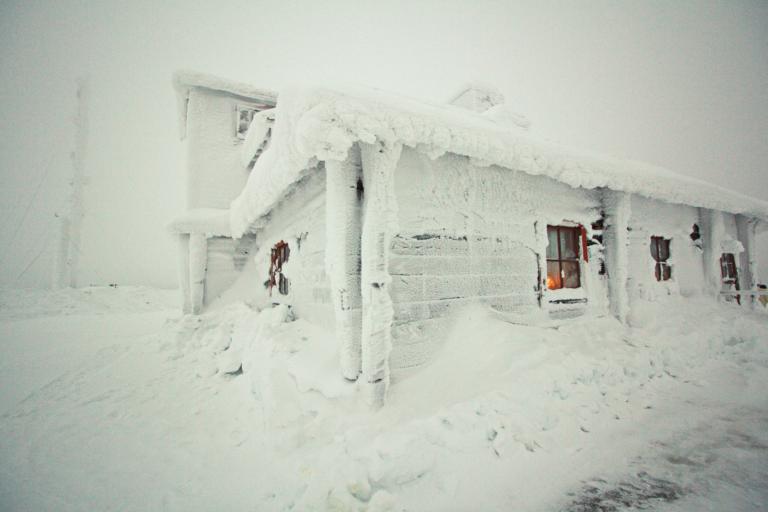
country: FI
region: Lapland
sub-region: Pohjois-Lappi
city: Ivalo
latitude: 68.4337
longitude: 27.4425
